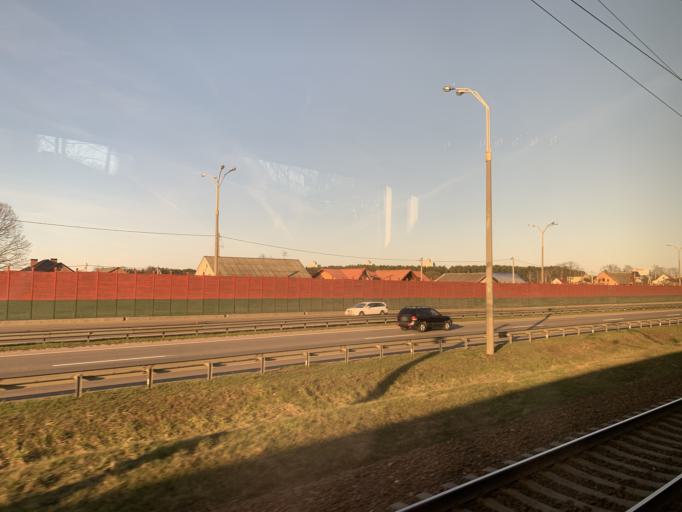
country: BY
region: Minsk
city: Zhdanovichy
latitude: 53.9512
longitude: 27.4142
